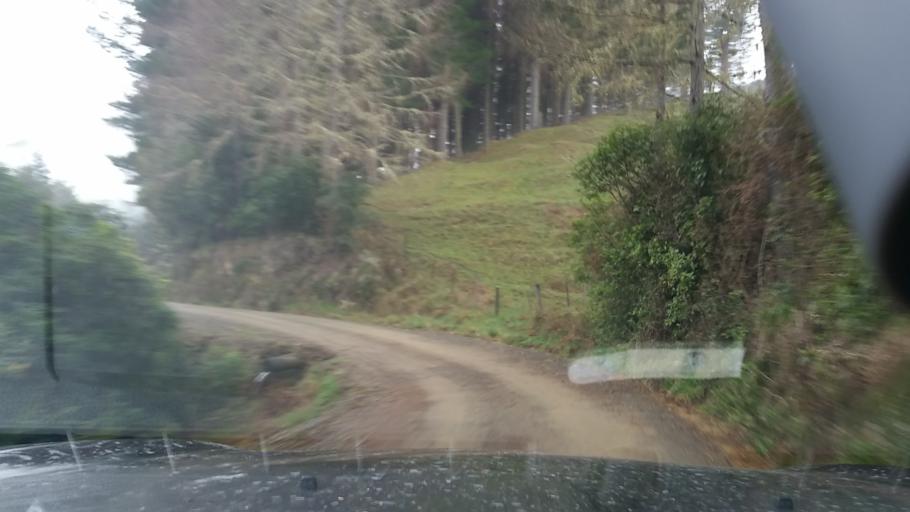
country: NZ
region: Nelson
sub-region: Nelson City
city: Nelson
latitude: -41.3734
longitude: 173.5997
